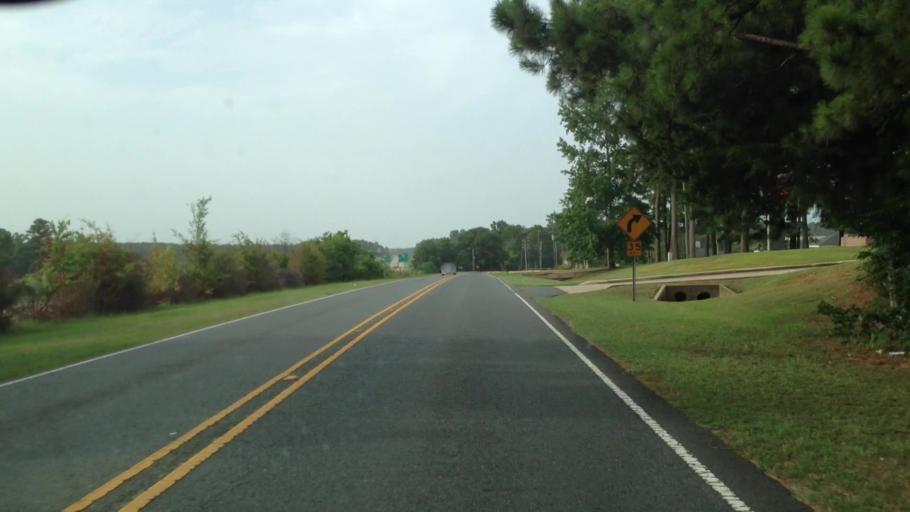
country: US
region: Louisiana
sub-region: Caddo Parish
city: Shreveport
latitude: 32.4494
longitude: -93.8437
